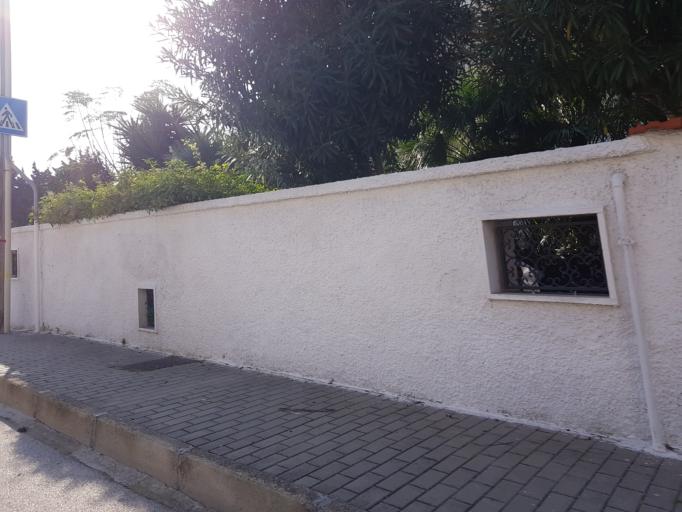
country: IT
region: Apulia
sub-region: Provincia di Brindisi
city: Materdomini
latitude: 40.6575
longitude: 17.9578
